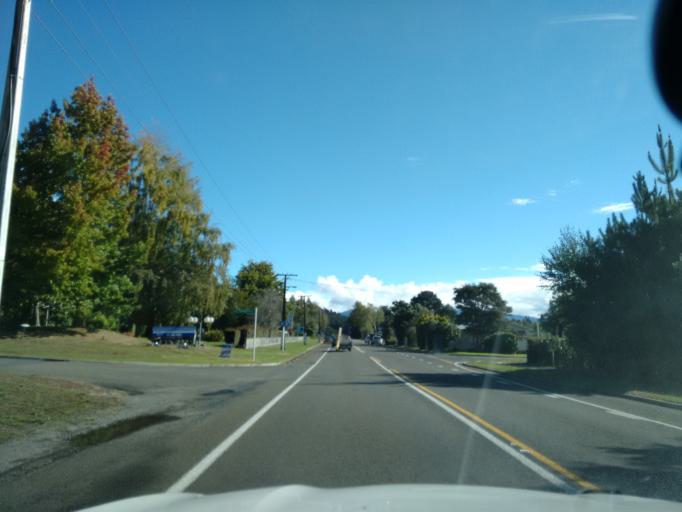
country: NZ
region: Waikato
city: Turangi
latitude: -38.9335
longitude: 175.8737
